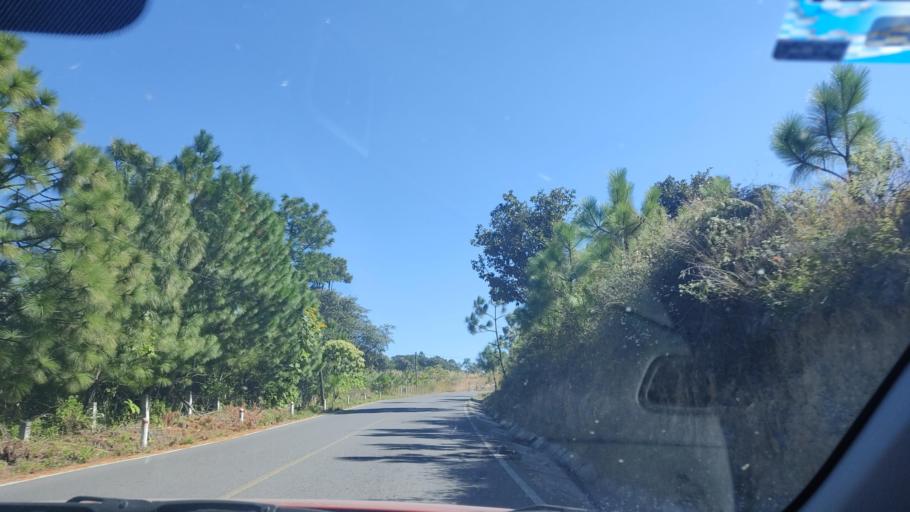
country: MX
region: Nayarit
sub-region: Jala
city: Rosa Blanca
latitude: 21.1010
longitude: -104.3701
